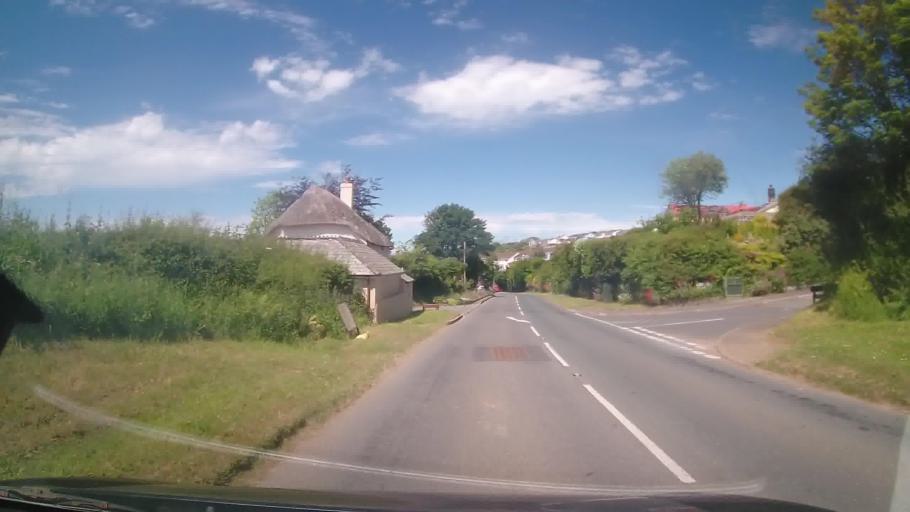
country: GB
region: England
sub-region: Devon
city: Kingsbridge
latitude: 50.2701
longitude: -3.7461
